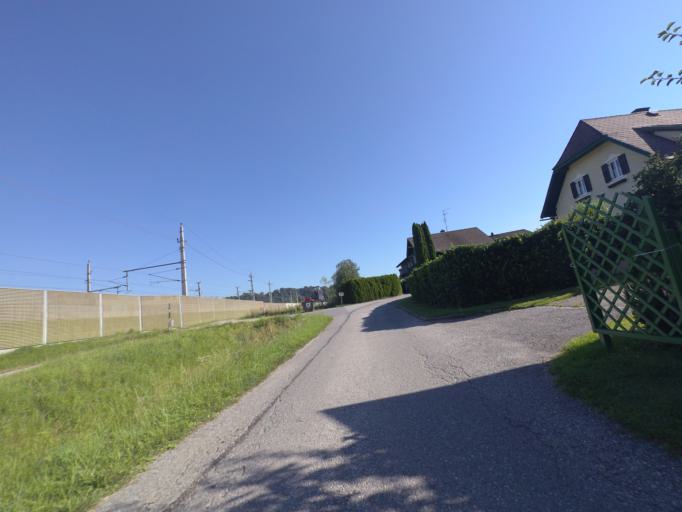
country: AT
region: Salzburg
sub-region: Politischer Bezirk Salzburg-Umgebung
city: Hallwang
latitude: 47.8614
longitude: 13.0960
